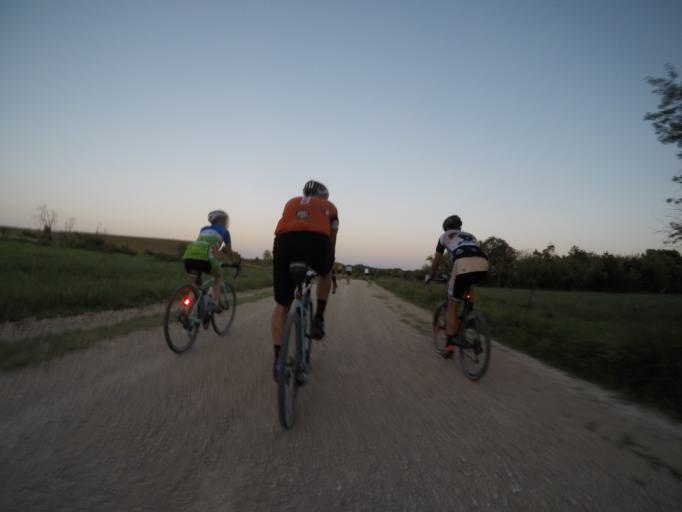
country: US
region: Kansas
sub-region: Riley County
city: Ogden
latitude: 38.9934
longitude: -96.5671
